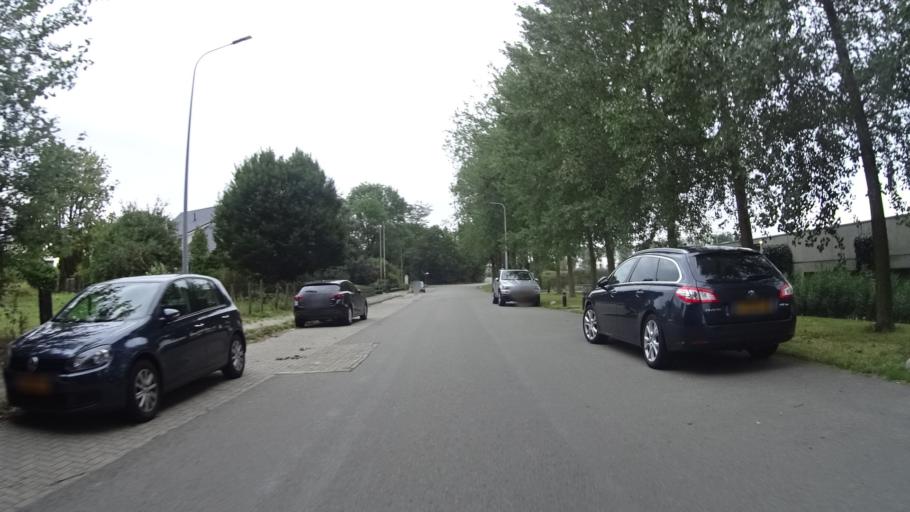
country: NL
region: Groningen
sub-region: Gemeente Groningen
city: Oosterpark
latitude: 53.2248
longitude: 6.6001
